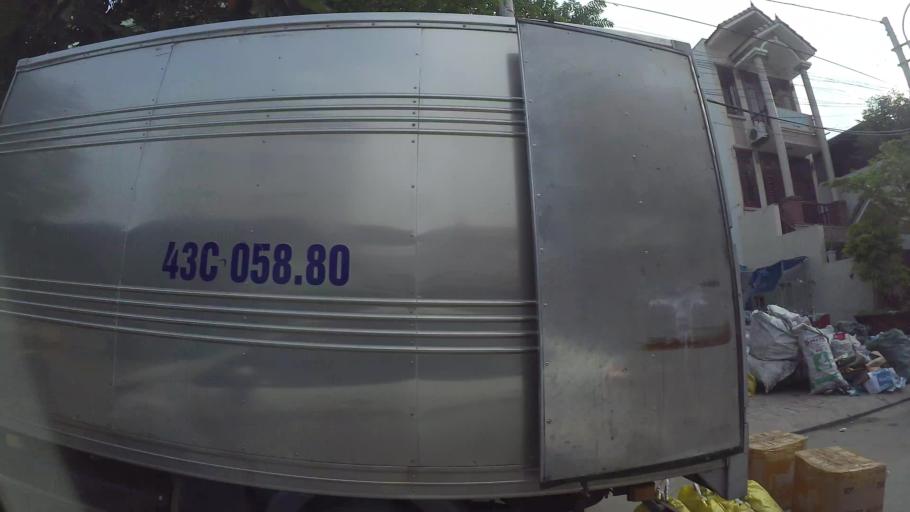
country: VN
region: Da Nang
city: Son Tra
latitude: 16.0637
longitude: 108.2392
